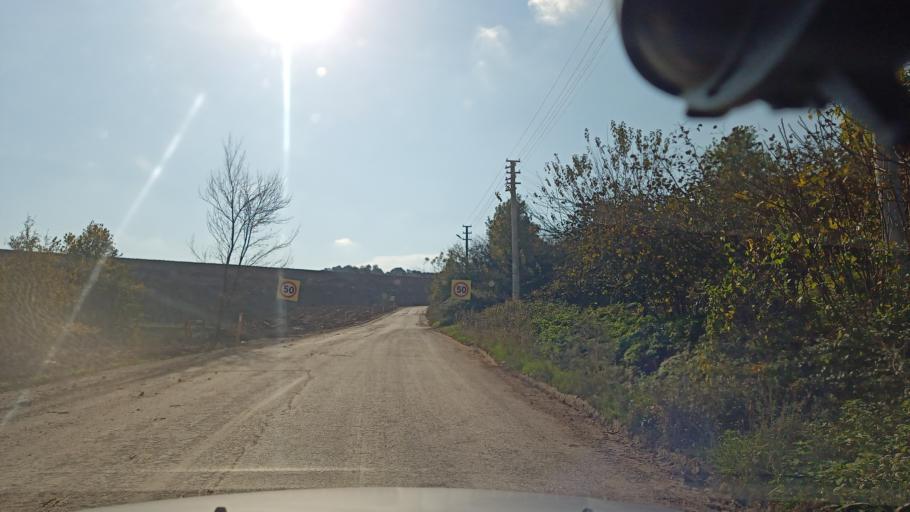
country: TR
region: Sakarya
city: Ferizli
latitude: 41.1042
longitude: 30.4762
